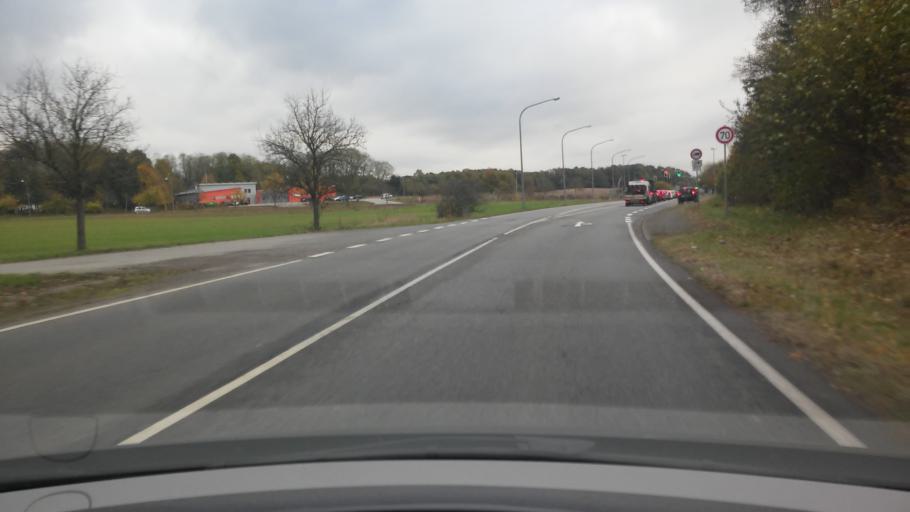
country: DE
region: Saarland
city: Wallerfangen
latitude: 49.3024
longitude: 6.7218
